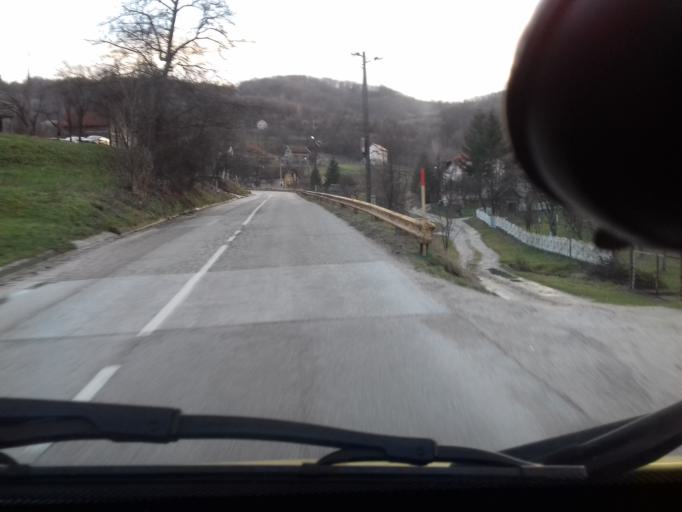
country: BA
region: Federation of Bosnia and Herzegovina
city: Lokvine
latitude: 44.1864
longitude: 17.8528
